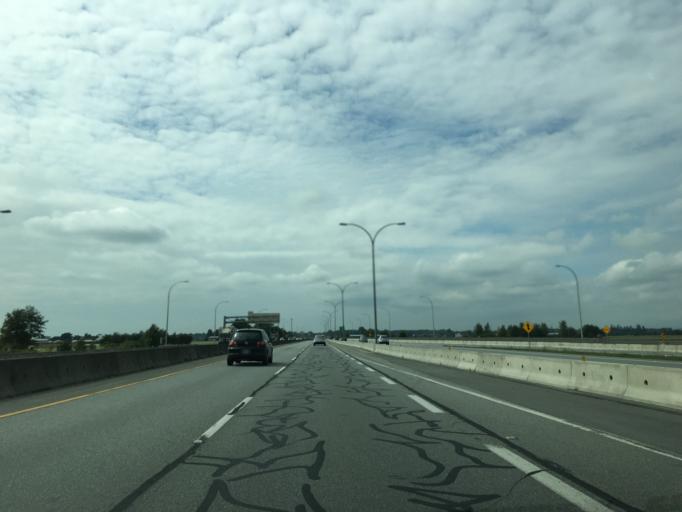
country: CA
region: British Columbia
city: Ladner
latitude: 49.0970
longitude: -123.0317
